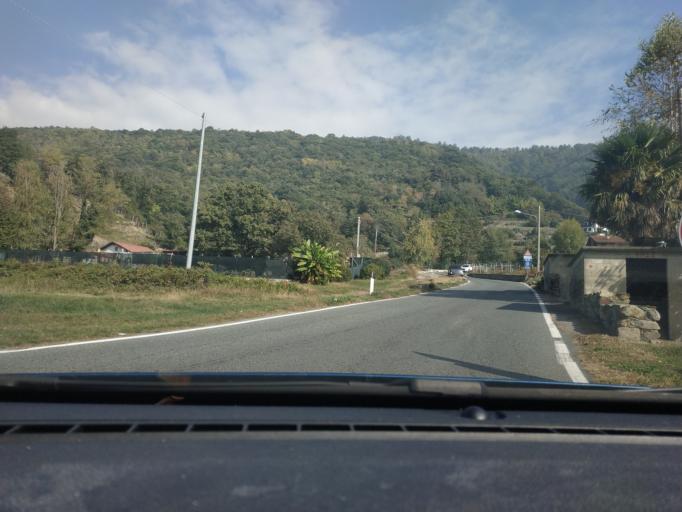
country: IT
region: Piedmont
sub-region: Provincia di Torino
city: Chiaverano
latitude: 45.5060
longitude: 7.9050
